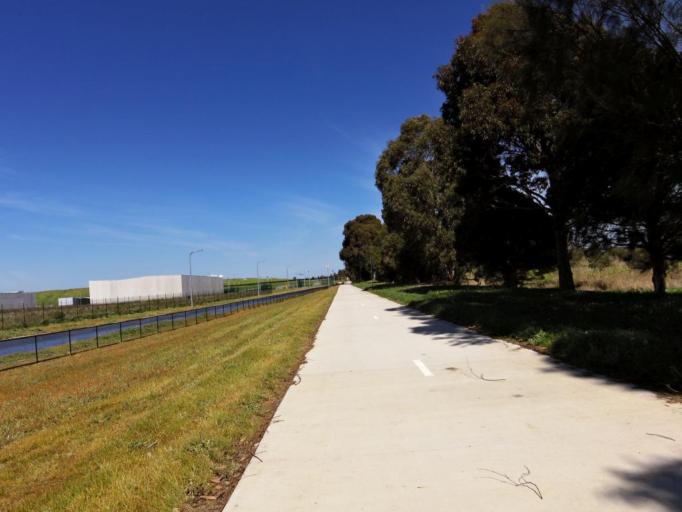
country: AU
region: Victoria
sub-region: Greater Dandenong
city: Keysborough
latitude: -38.0055
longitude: 145.1923
